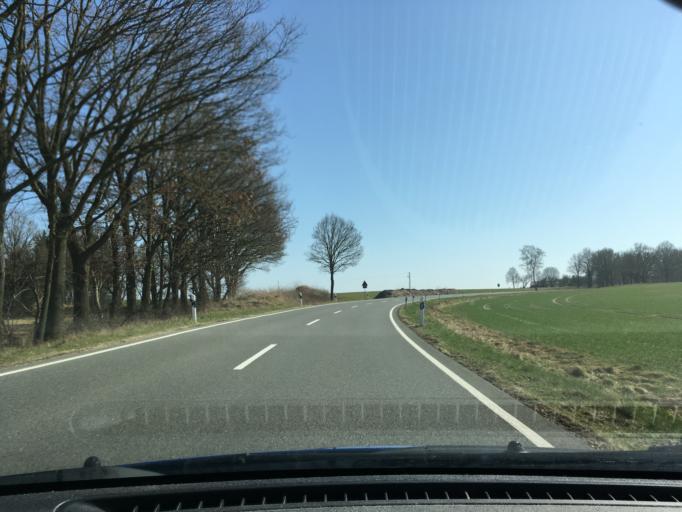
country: DE
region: Lower Saxony
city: Rehlingen
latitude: 53.1045
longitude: 10.2589
